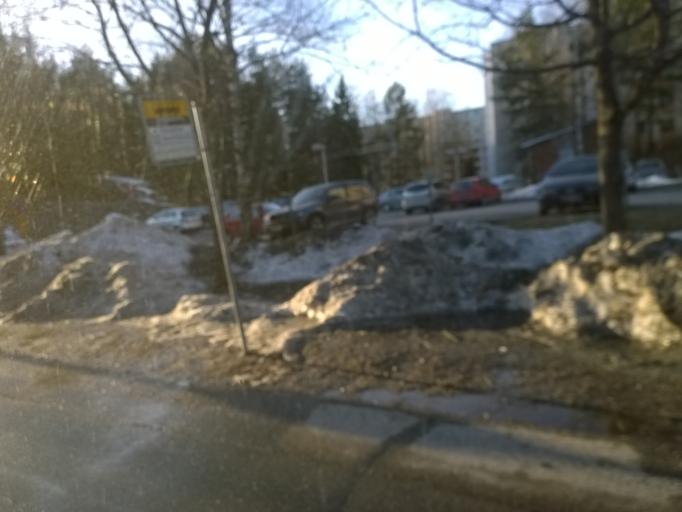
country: FI
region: Pirkanmaa
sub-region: Tampere
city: Tampere
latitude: 61.4499
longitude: 23.8440
